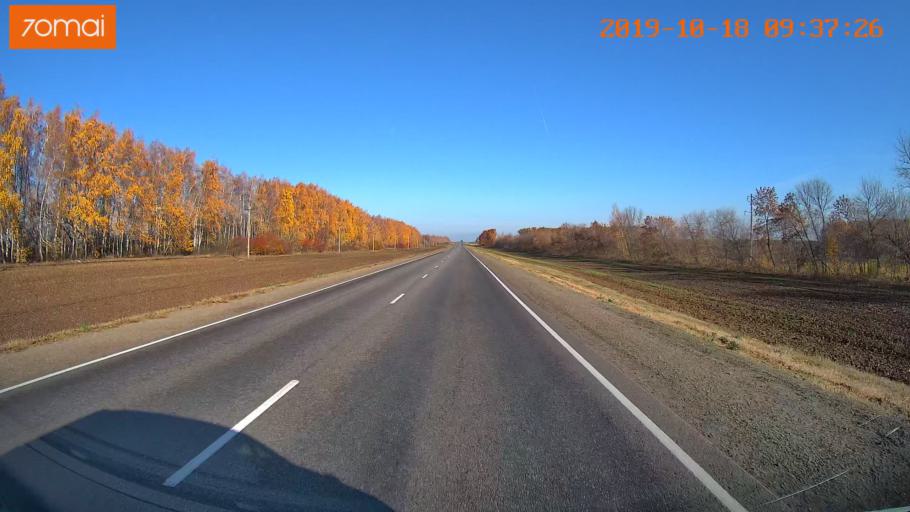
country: RU
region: Tula
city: Yefremov
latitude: 53.2222
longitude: 38.1411
